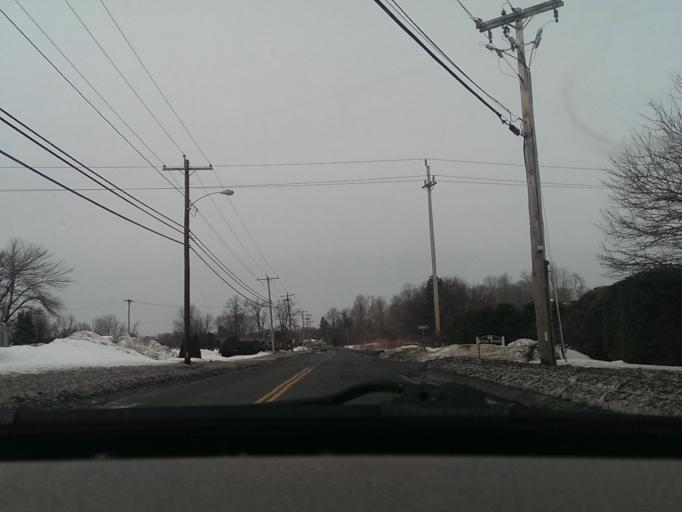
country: US
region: Massachusetts
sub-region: Hampden County
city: East Longmeadow
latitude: 42.0498
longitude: -72.5193
